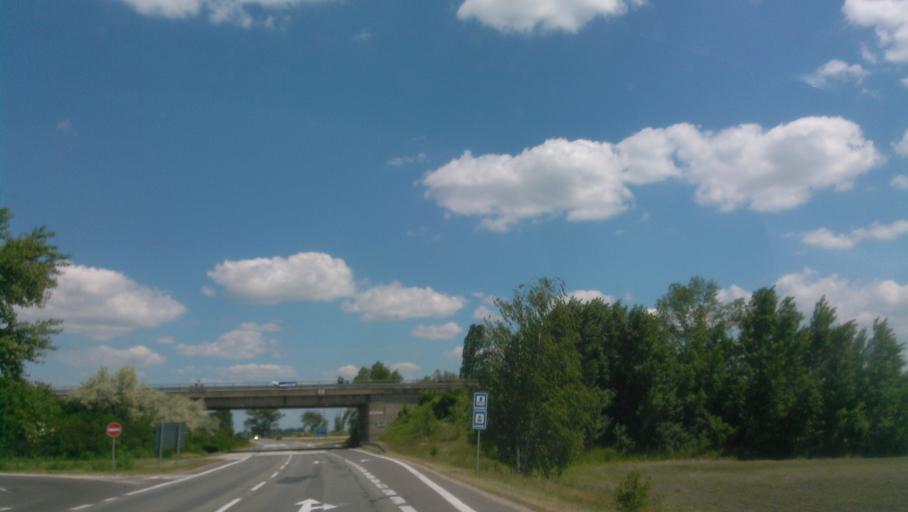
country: SK
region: Trnavsky
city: Dunajska Streda
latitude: 47.9757
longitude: 17.6077
